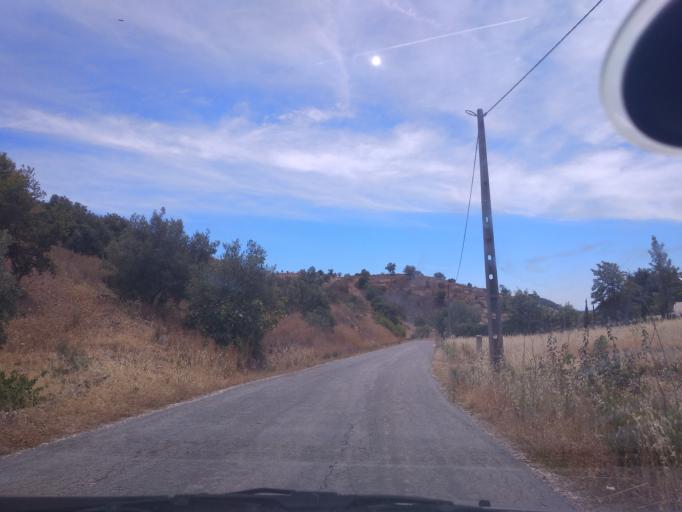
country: PT
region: Faro
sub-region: Sao Bras de Alportel
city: Sao Bras de Alportel
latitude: 37.1715
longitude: -7.8049
